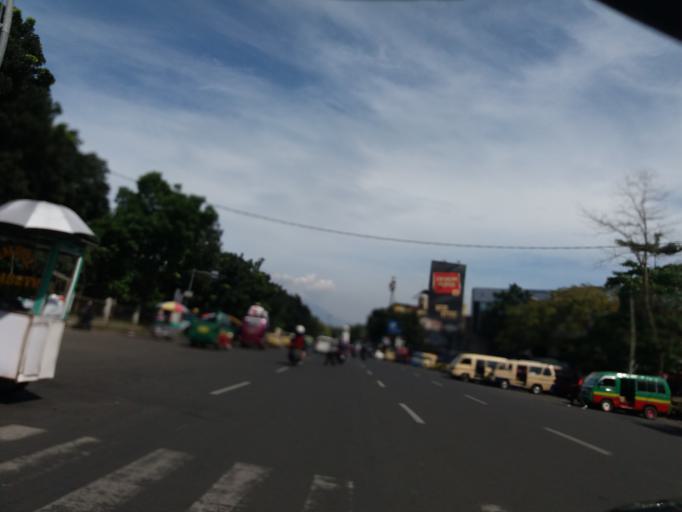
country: ID
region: West Java
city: Bandung
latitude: -6.9336
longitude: 107.6033
